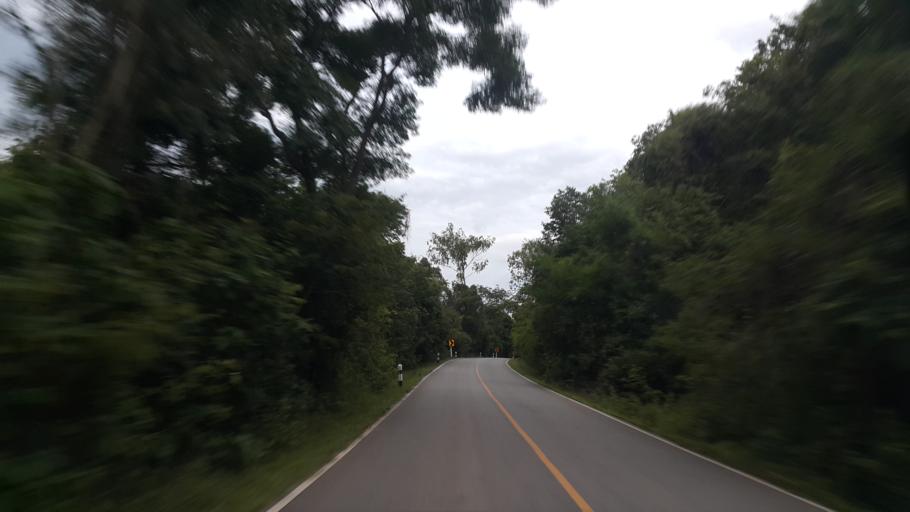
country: TH
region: Loei
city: Na Haeo
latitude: 17.5302
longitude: 101.1975
